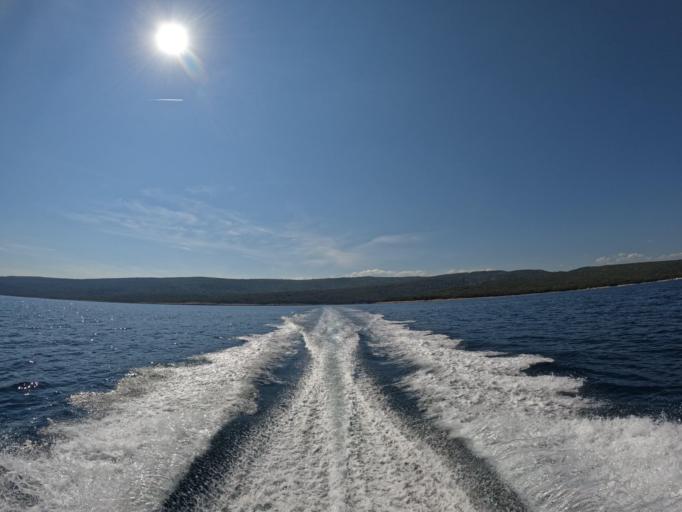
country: HR
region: Primorsko-Goranska
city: Cres
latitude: 44.9458
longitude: 14.4808
